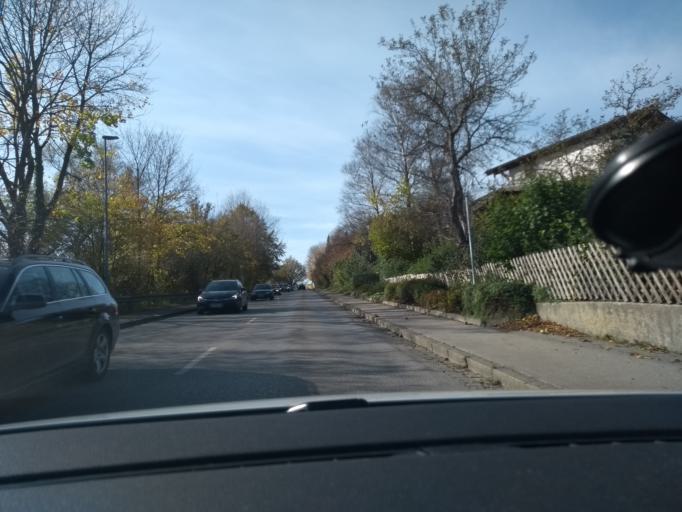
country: DE
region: Bavaria
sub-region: Upper Bavaria
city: Bad Endorf
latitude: 47.9065
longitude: 12.2910
